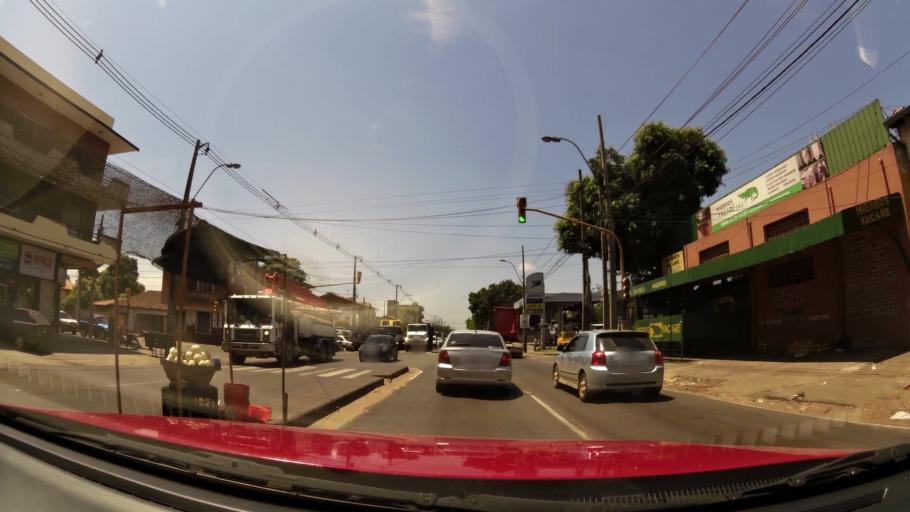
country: PY
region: Central
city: Fernando de la Mora
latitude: -25.3243
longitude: -57.5656
